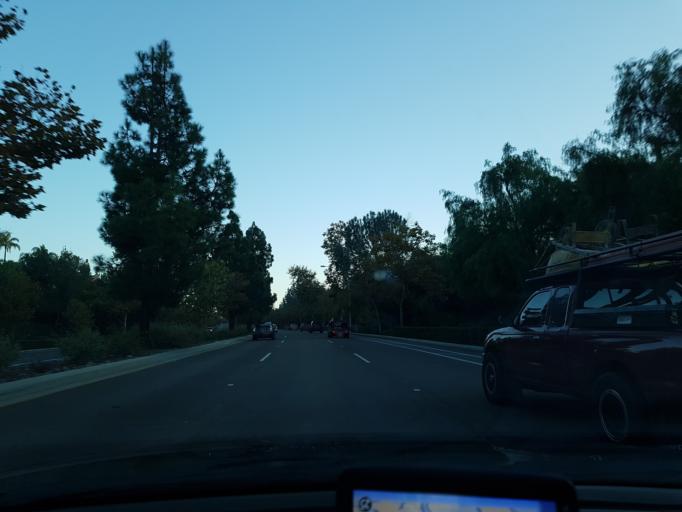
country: US
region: California
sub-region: San Diego County
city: Fairbanks Ranch
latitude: 32.9314
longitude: -117.1259
